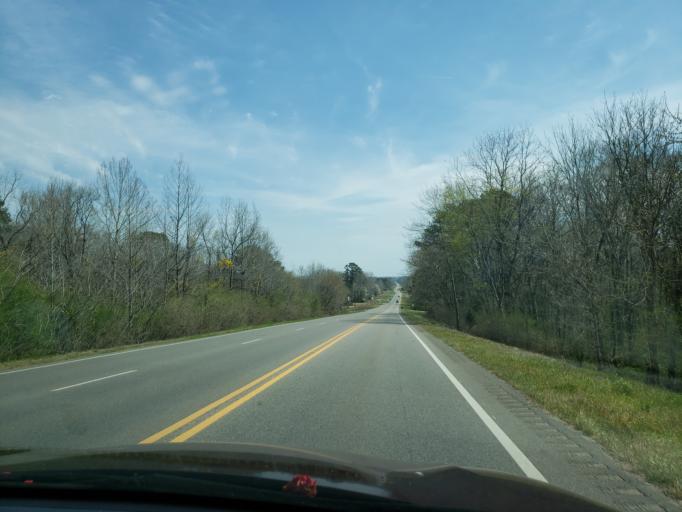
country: US
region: Alabama
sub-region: Autauga County
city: Prattville
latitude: 32.4306
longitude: -86.5289
